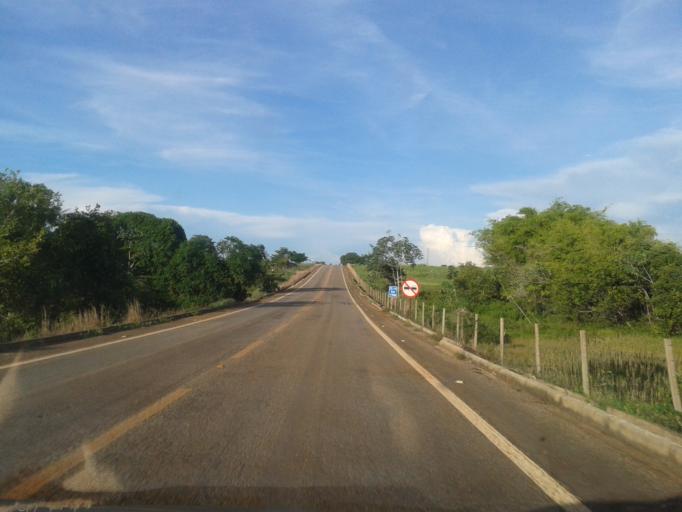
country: BR
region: Goias
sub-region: Sao Miguel Do Araguaia
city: Sao Miguel do Araguaia
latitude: -13.4388
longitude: -50.2872
